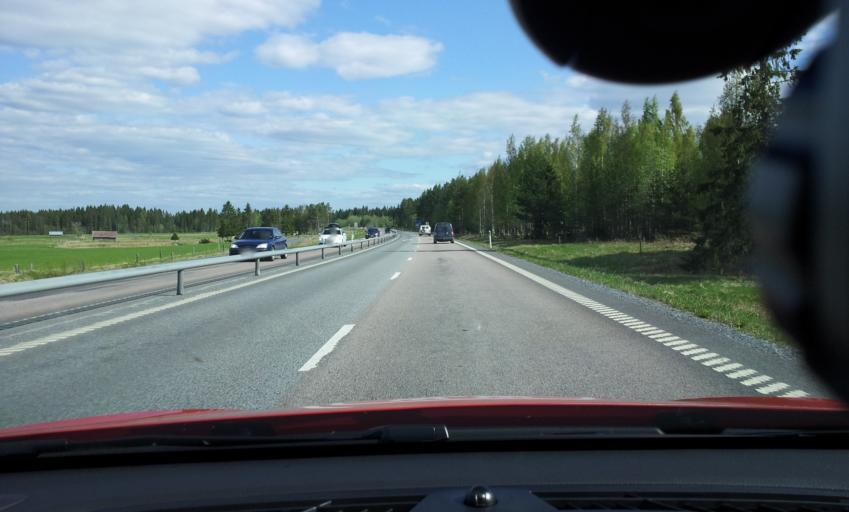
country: SE
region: Jaemtland
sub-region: OEstersunds Kommun
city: Ostersund
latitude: 63.2592
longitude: 14.5527
